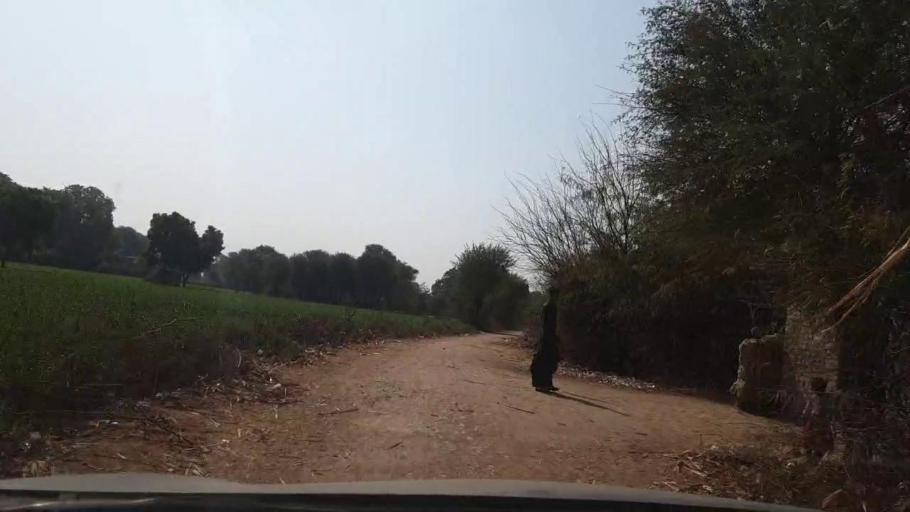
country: PK
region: Sindh
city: Tando Allahyar
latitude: 25.5339
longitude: 68.7687
